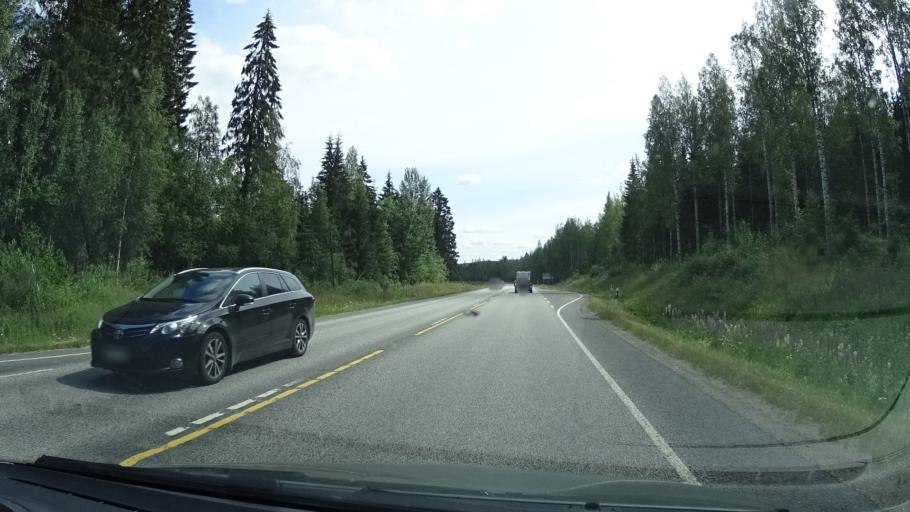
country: FI
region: Central Finland
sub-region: Jyvaeskylae
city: Jyvaeskylae
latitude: 62.2626
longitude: 25.5895
